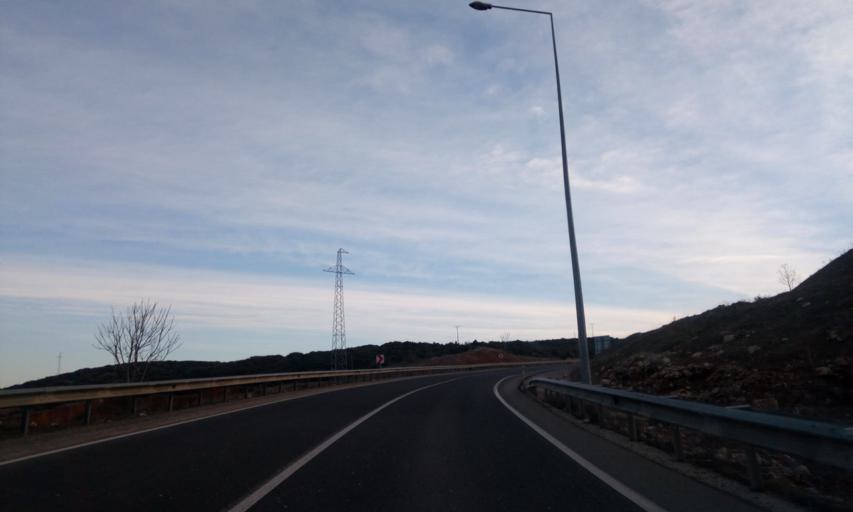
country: TR
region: Bilecik
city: Kuplu
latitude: 40.1218
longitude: 30.0141
